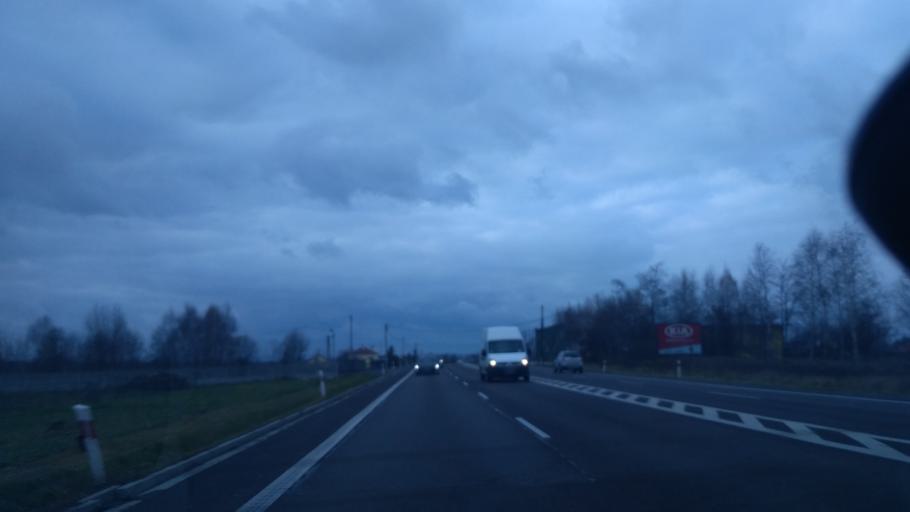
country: PL
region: Subcarpathian Voivodeship
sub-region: Powiat rzeszowski
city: Krasne
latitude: 50.0422
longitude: 22.1085
